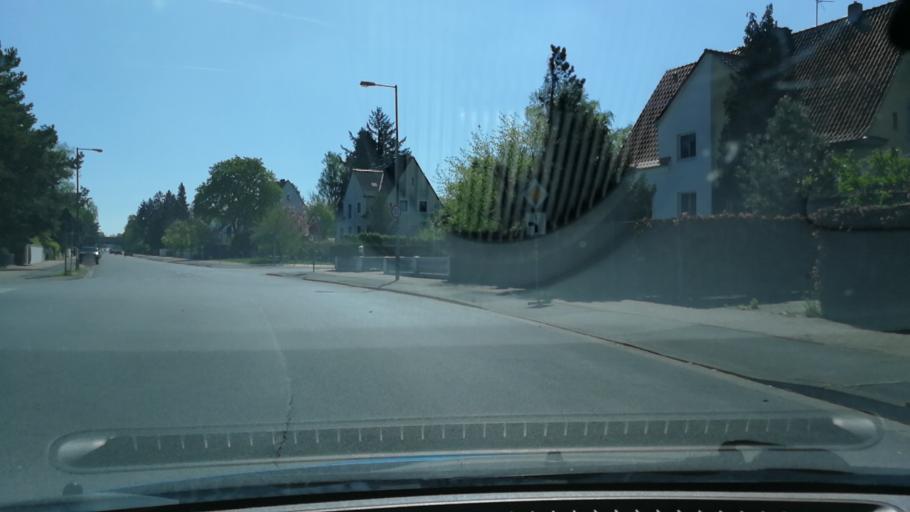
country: DE
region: Lower Saxony
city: Laatzen
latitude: 52.3564
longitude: 9.8193
